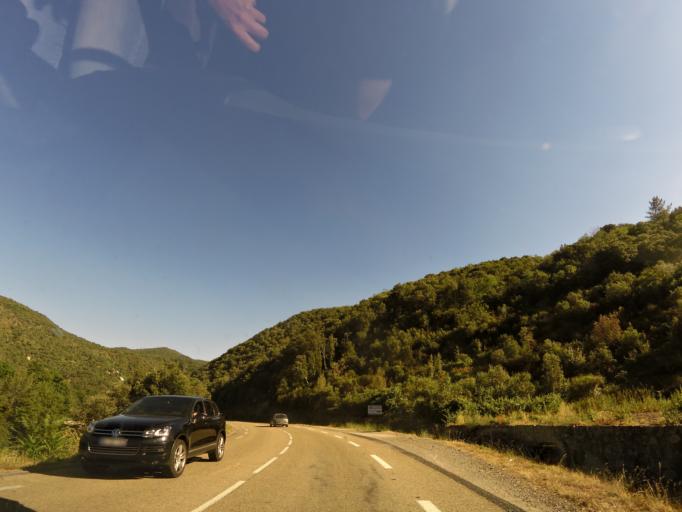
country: FR
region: Languedoc-Roussillon
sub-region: Departement du Gard
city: Valleraugue
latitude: 44.0314
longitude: 3.6786
